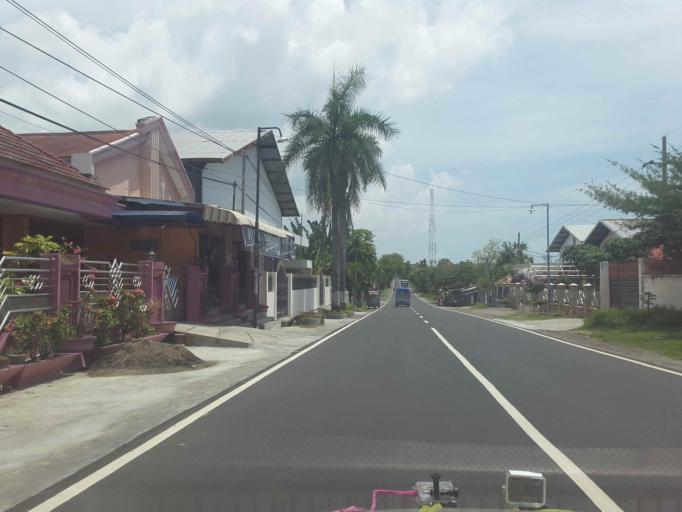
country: ID
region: East Java
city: Biyan
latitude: -7.1140
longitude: 113.7262
